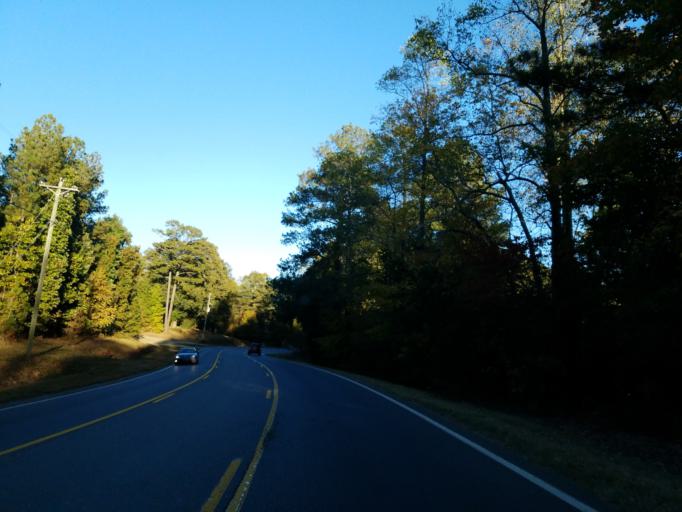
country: US
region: Georgia
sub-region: Dawson County
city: Dawsonville
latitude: 34.3776
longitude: -84.0506
